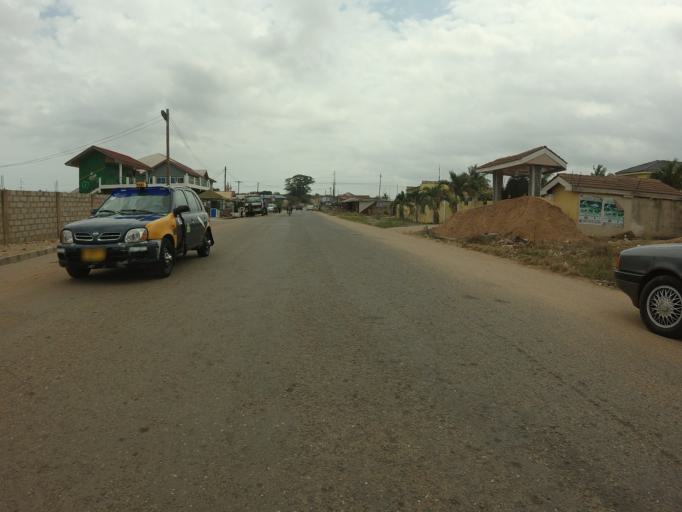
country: GH
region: Greater Accra
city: Dome
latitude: 5.6523
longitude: -0.2598
